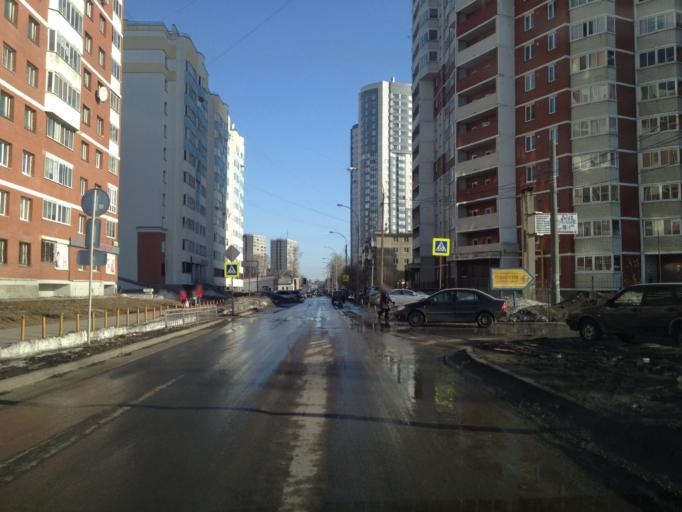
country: RU
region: Sverdlovsk
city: Yekaterinburg
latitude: 56.8736
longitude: 60.5430
